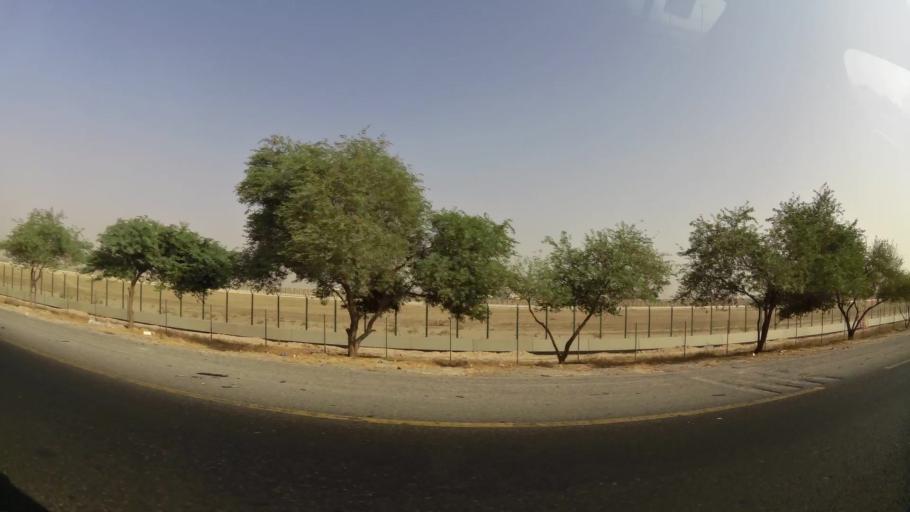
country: KW
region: Al Farwaniyah
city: Janub as Surrah
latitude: 29.1829
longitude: 47.9622
